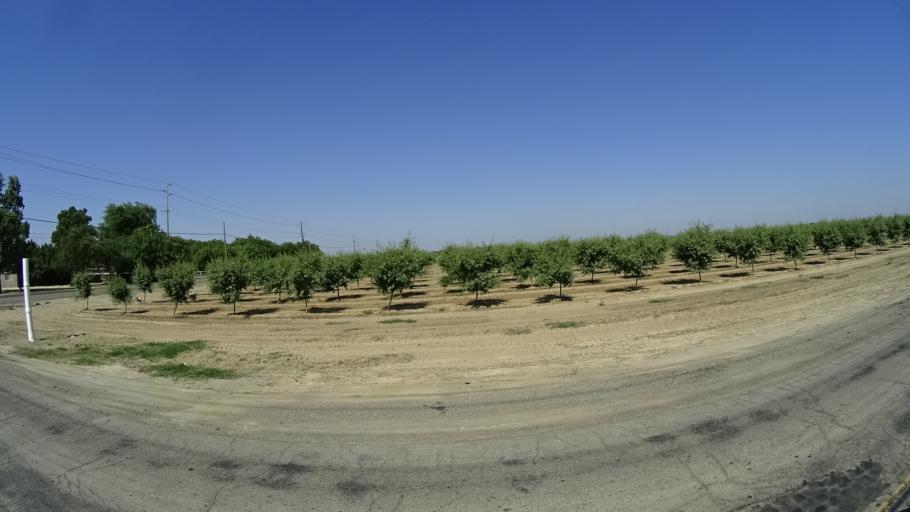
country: US
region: California
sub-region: Kings County
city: Hanford
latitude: 36.3430
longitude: -119.5831
